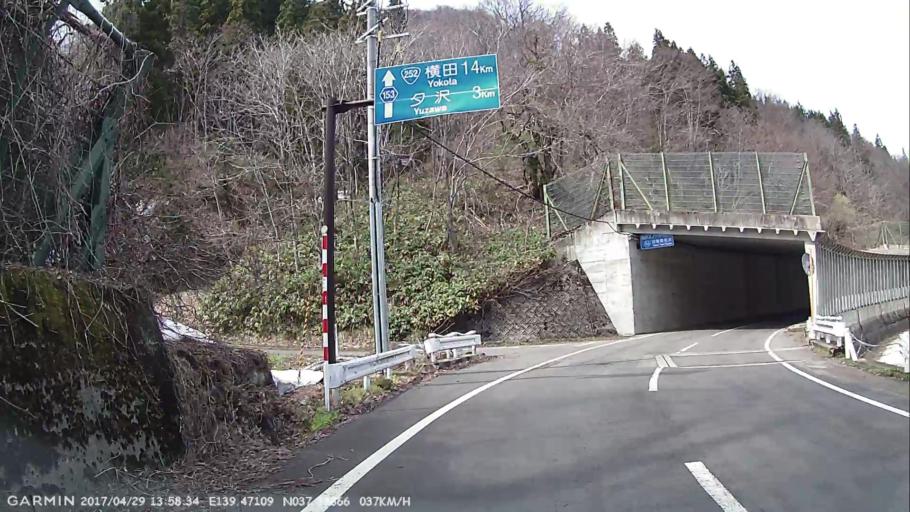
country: JP
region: Niigata
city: Muramatsu
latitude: 37.3387
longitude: 139.4711
